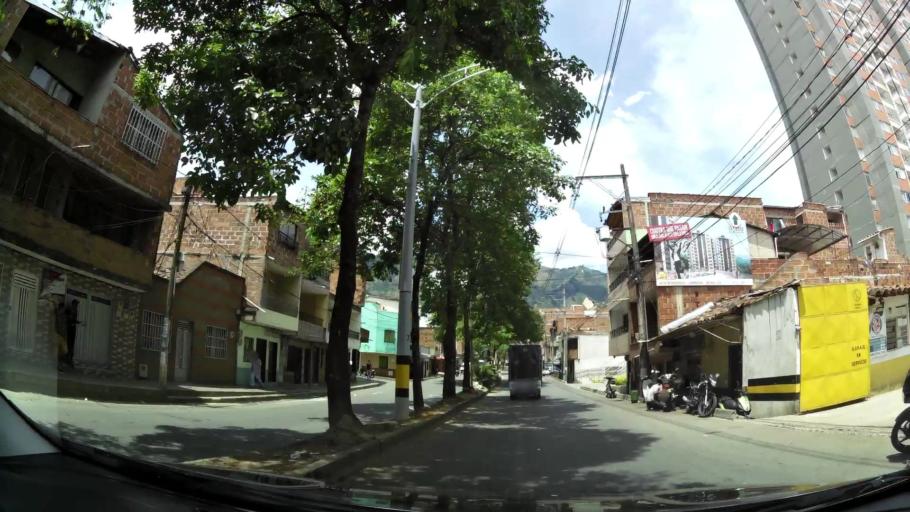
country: CO
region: Antioquia
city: Bello
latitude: 6.3415
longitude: -75.5654
